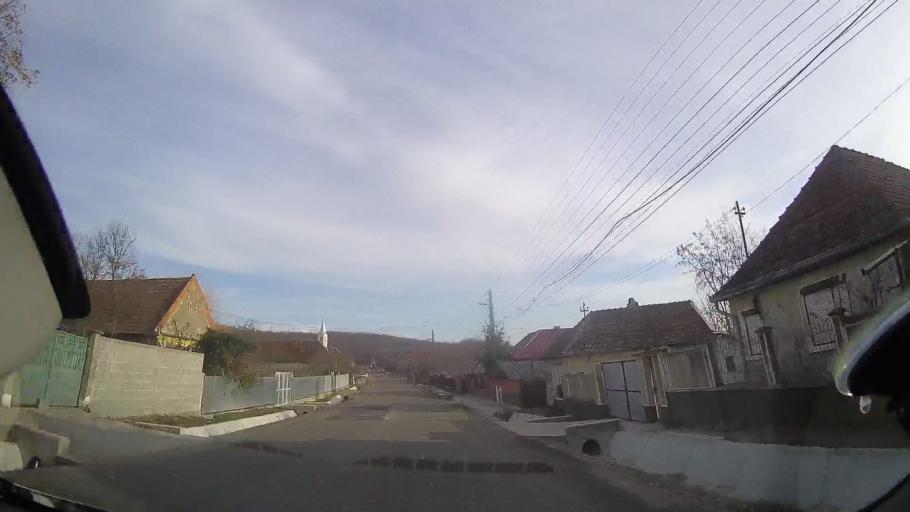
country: RO
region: Bihor
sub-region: Comuna Sarbi
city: Sarbi
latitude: 47.1768
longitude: 22.1478
